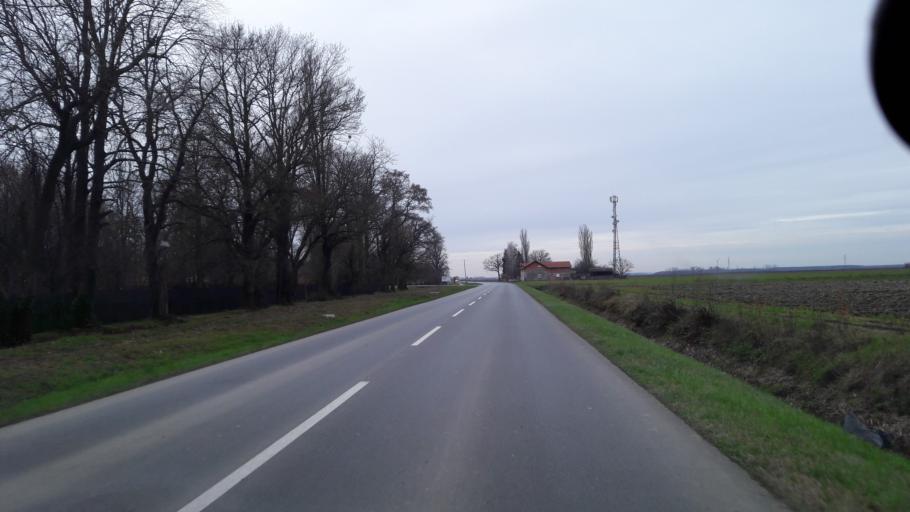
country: HR
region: Osjecko-Baranjska
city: Ovcara
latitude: 45.5060
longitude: 18.5636
